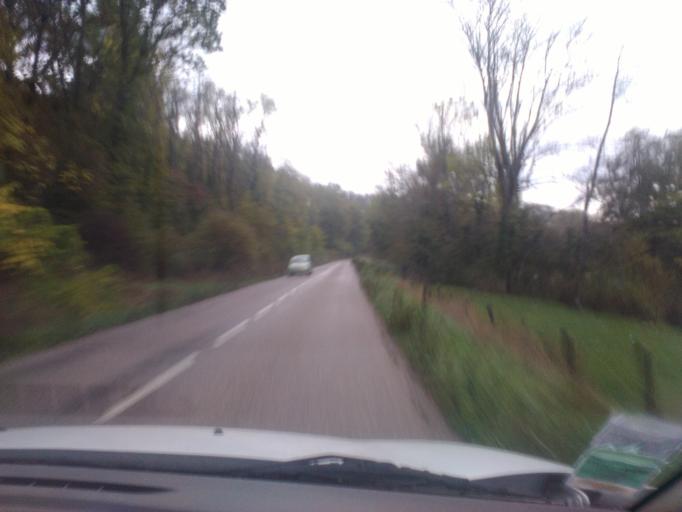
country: FR
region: Lorraine
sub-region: Departement des Vosges
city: Chatel-sur-Moselle
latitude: 48.2969
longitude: 6.4286
